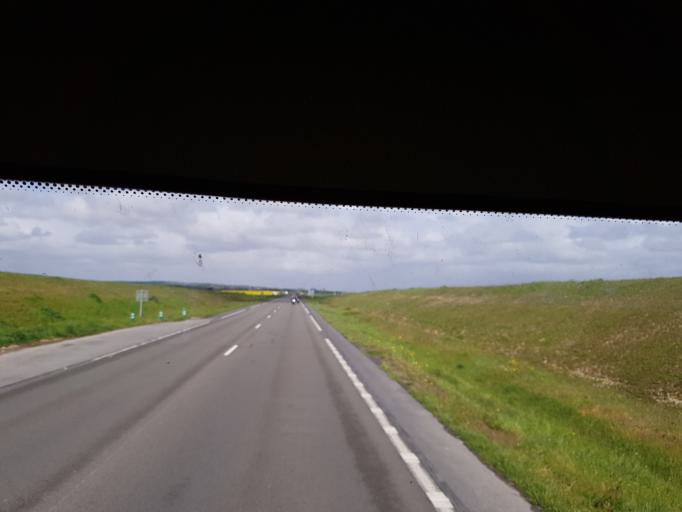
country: FR
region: Nord-Pas-de-Calais
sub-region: Departement du Nord
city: Proville
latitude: 50.1449
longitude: 3.2079
